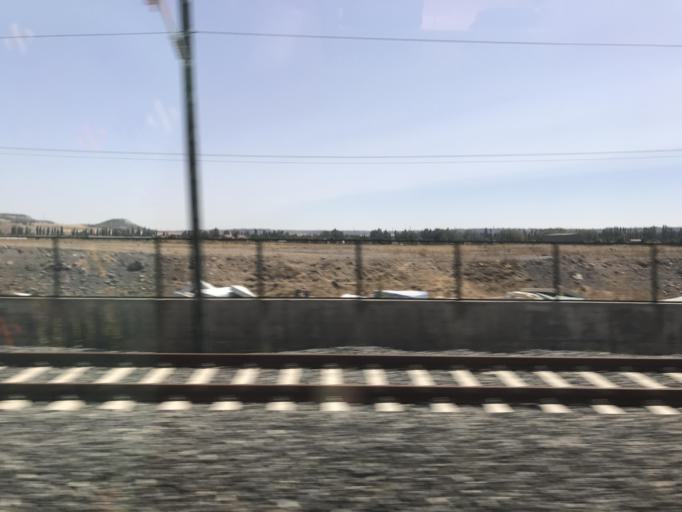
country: ES
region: Castille and Leon
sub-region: Provincia de Valladolid
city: Santovenia de Pisuerga
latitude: 41.6721
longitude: -4.6957
